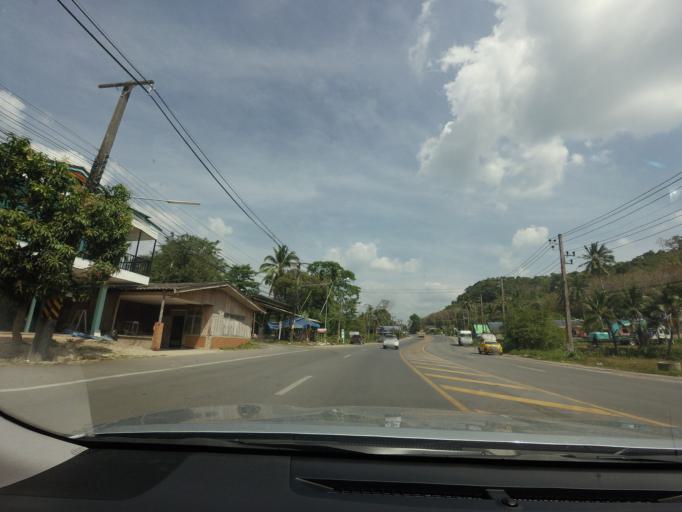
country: TH
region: Phangnga
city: Ban Ao Nang
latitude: 8.0524
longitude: 98.7671
